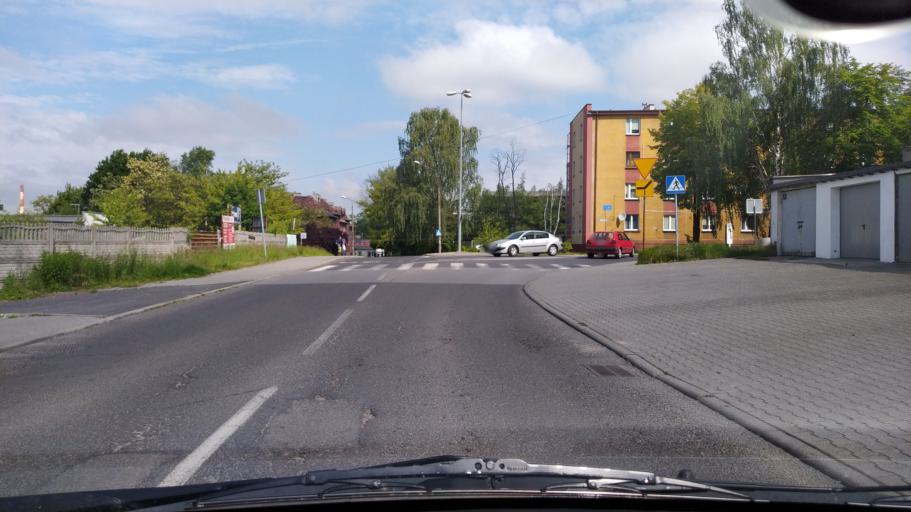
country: PL
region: Silesian Voivodeship
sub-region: Powiat gliwicki
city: Przyszowice
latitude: 50.2858
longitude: 18.7269
